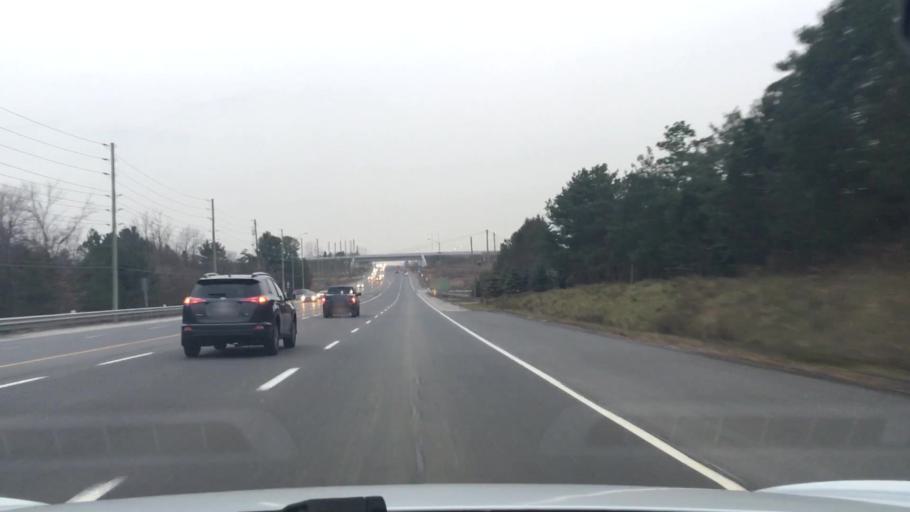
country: CA
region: Ontario
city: Ajax
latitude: 43.9444
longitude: -78.9998
